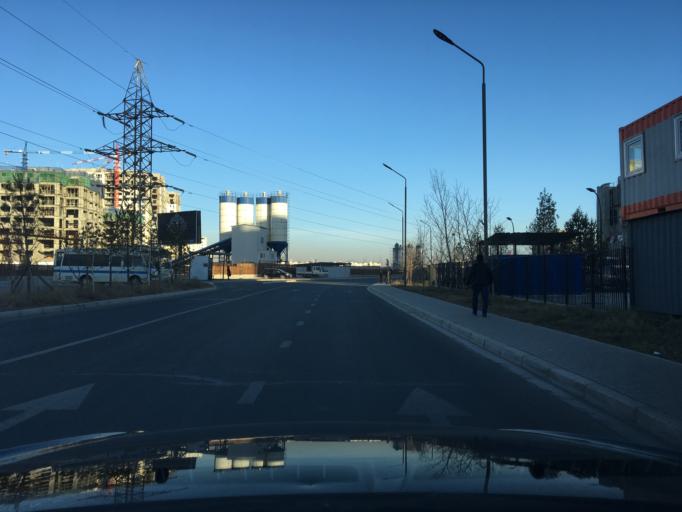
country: MN
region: Ulaanbaatar
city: Ulaanbaatar
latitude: 47.8927
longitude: 106.9238
